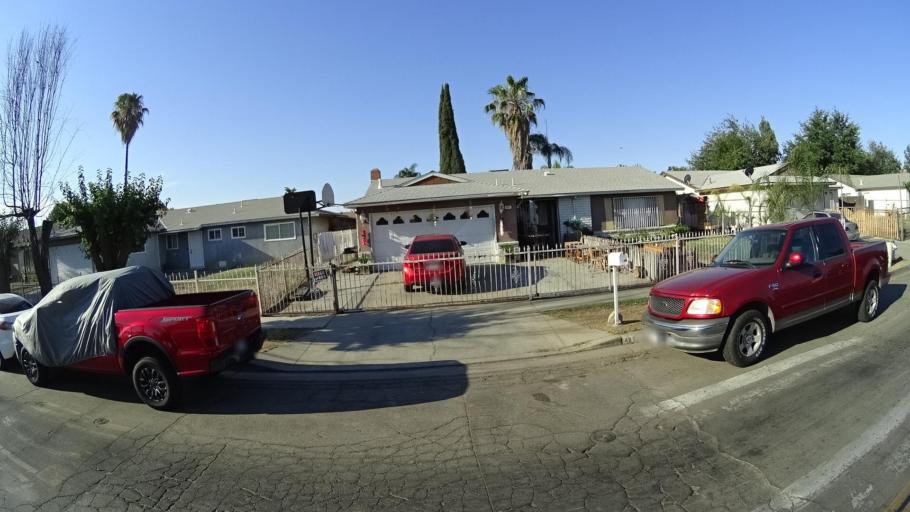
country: US
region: California
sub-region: Fresno County
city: Fresno
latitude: 36.7178
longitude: -119.7414
